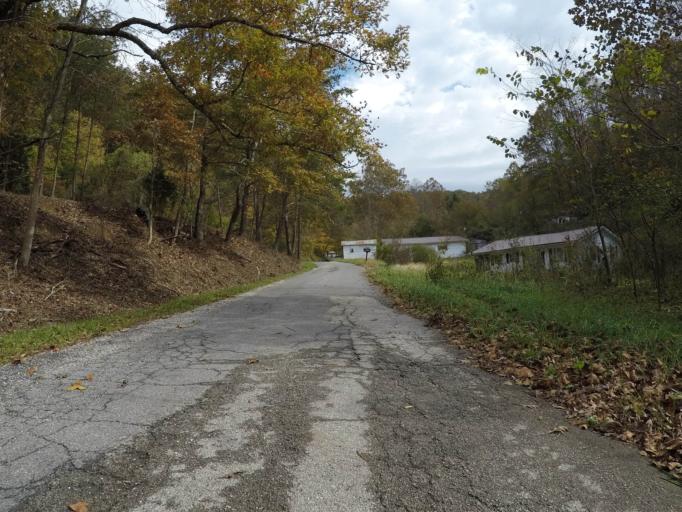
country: US
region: West Virginia
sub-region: Wayne County
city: Lavalette
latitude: 38.3460
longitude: -82.4471
